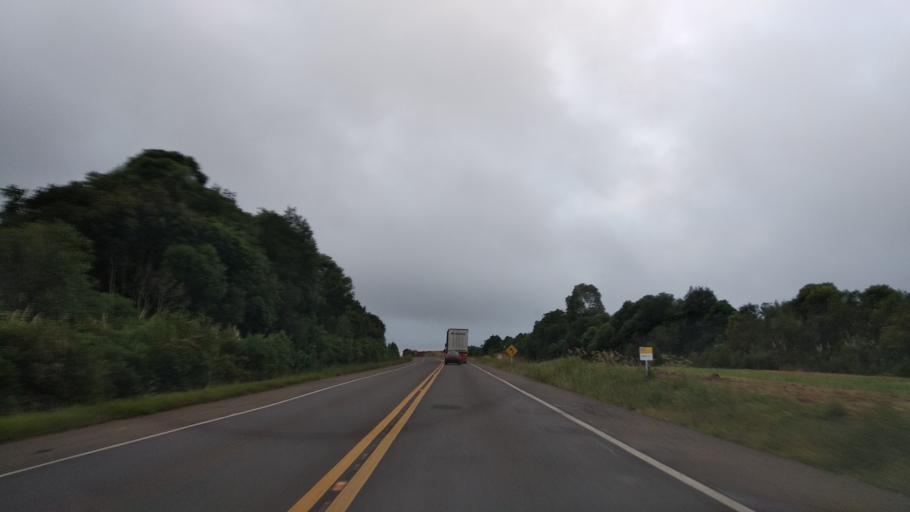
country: BR
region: Santa Catarina
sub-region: Campos Novos
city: Campos Novos
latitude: -27.3845
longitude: -51.1063
